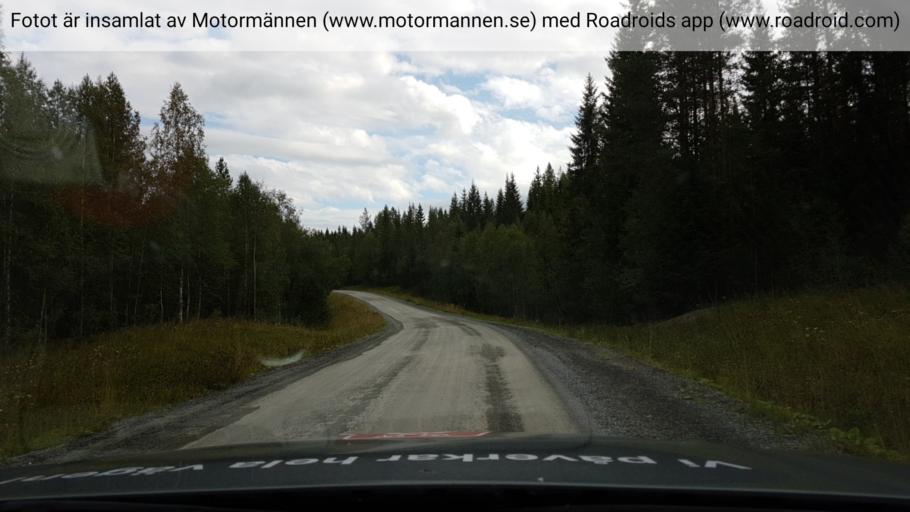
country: SE
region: Jaemtland
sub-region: Krokoms Kommun
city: Valla
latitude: 63.6716
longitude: 13.6984
